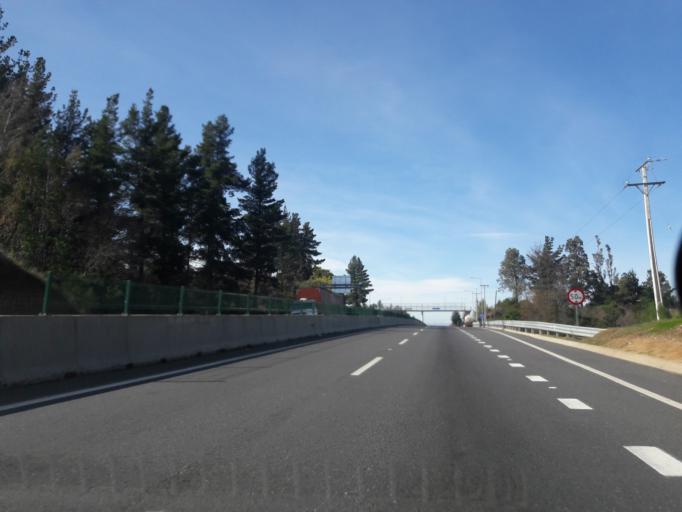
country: CL
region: Biobio
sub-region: Provincia de Biobio
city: Yumbel
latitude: -36.9630
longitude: -72.7118
